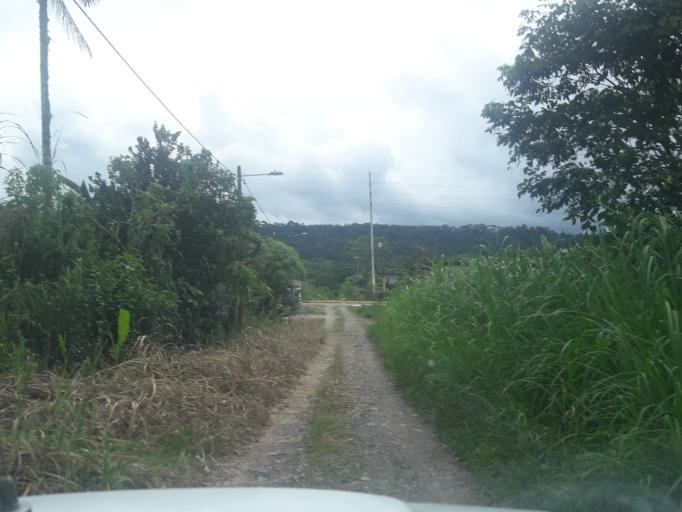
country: EC
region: Napo
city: Tena
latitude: -0.9568
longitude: -77.8151
